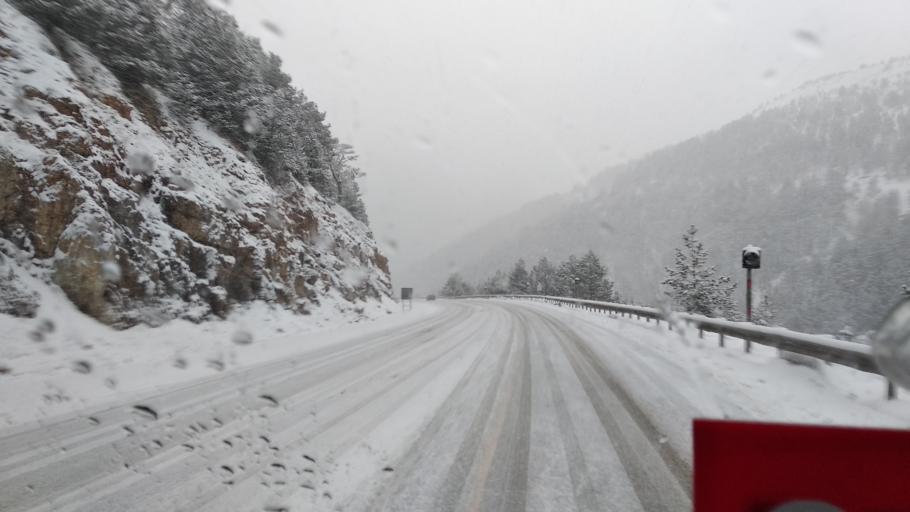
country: TR
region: Gumushane
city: Torul
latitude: 40.6558
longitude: 39.4033
